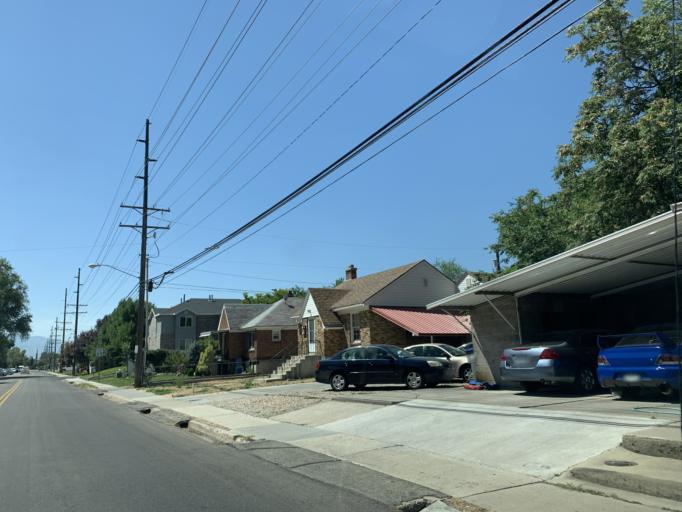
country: US
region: Utah
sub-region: Utah County
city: Provo
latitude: 40.2382
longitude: -111.6466
